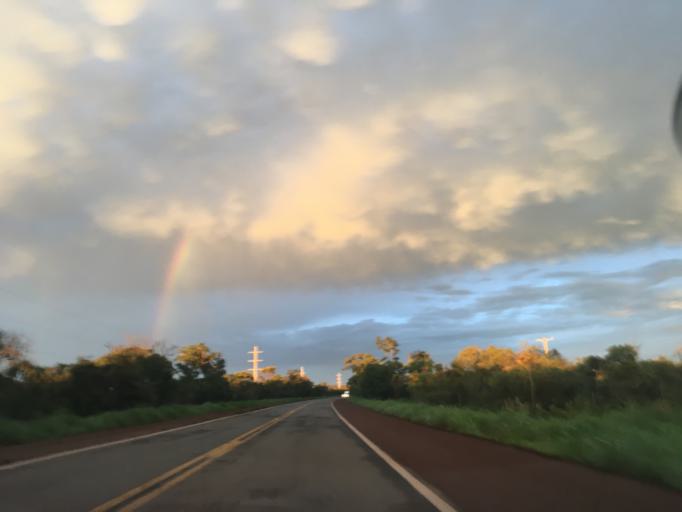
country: BR
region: Federal District
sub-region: Brasilia
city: Brasilia
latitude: -15.9840
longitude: -47.9363
